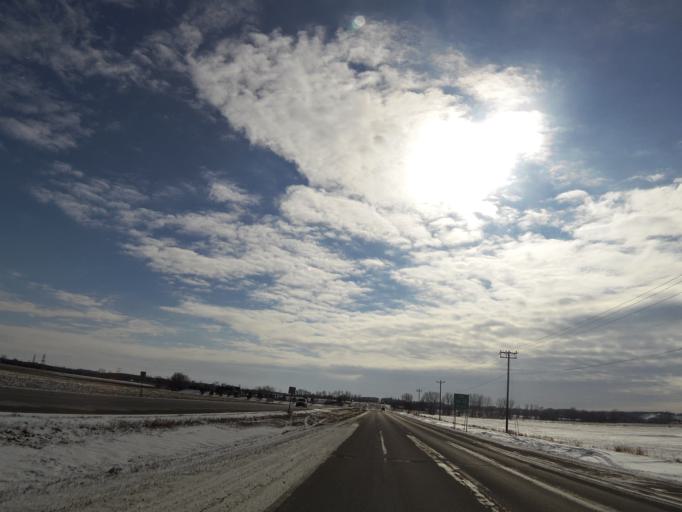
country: US
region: Minnesota
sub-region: Washington County
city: Lake Elmo
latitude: 44.9559
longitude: -92.8626
